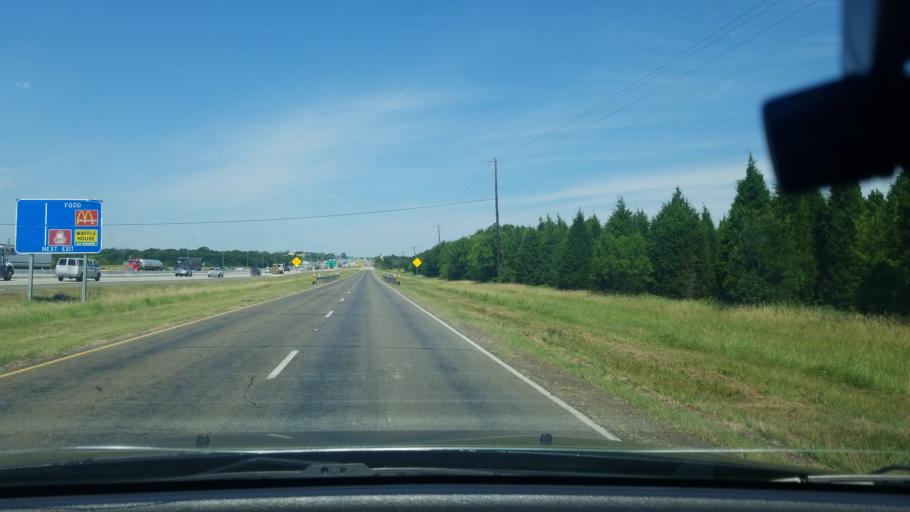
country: US
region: Texas
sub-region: Dallas County
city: Sunnyvale
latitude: 32.7889
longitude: -96.5838
